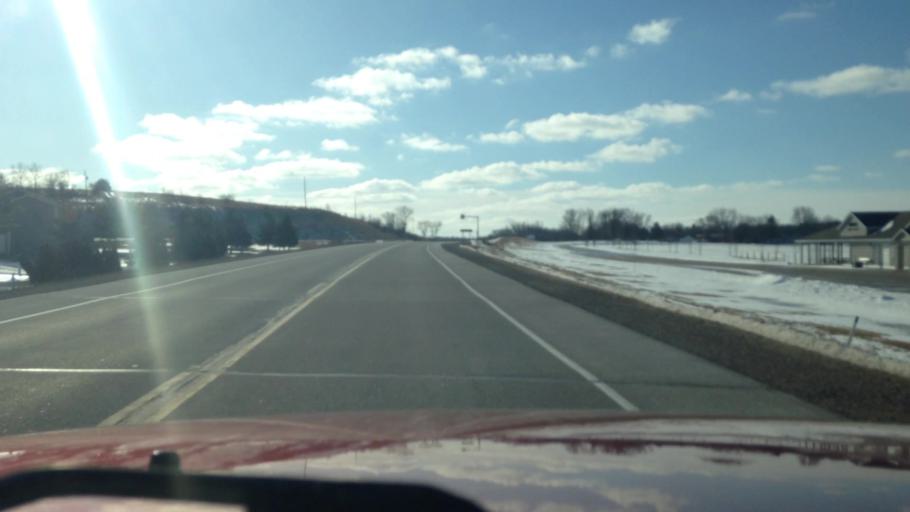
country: US
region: Wisconsin
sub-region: Waukesha County
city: Oconomowoc
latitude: 43.1692
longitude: -88.5036
